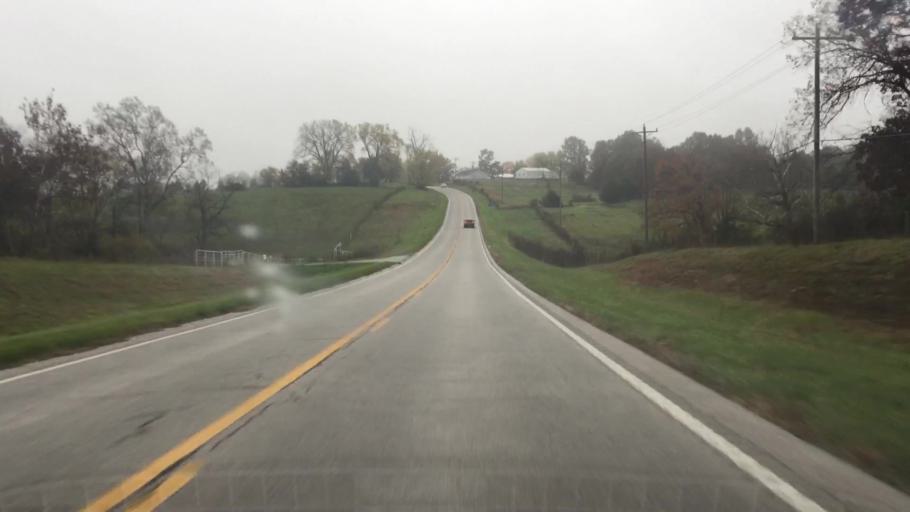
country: US
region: Missouri
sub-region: Callaway County
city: Fulton
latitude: 38.8602
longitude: -92.0003
